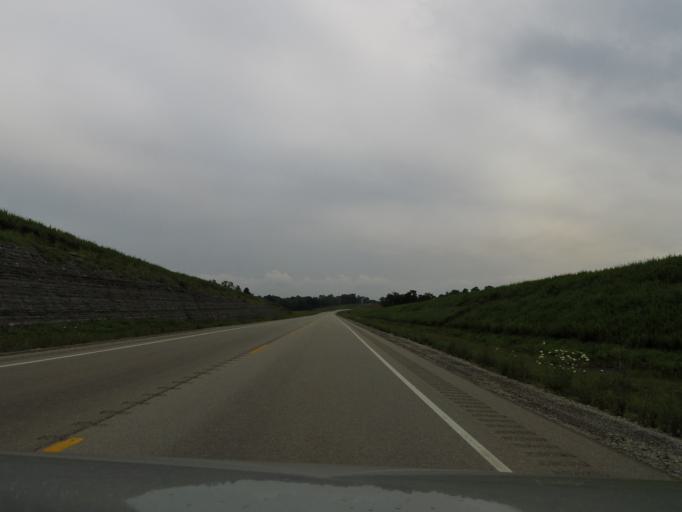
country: US
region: Ohio
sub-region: Brown County
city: Aberdeen
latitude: 38.6017
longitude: -83.8245
